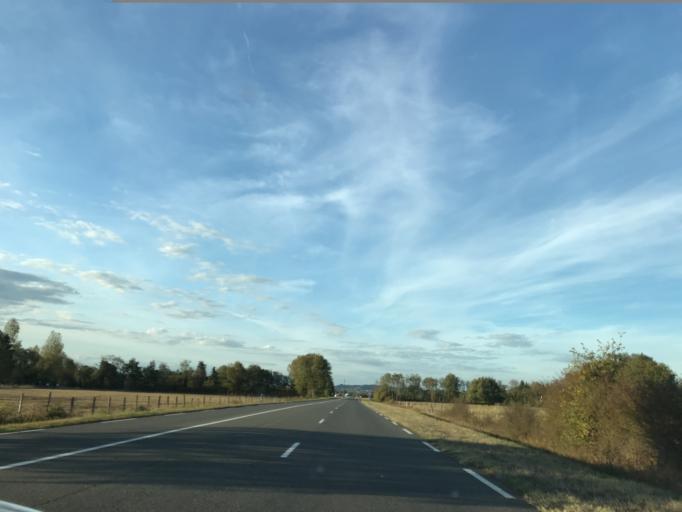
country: FR
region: Auvergne
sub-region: Departement de l'Allier
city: Saint-Yorre
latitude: 46.0240
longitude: 3.4793
